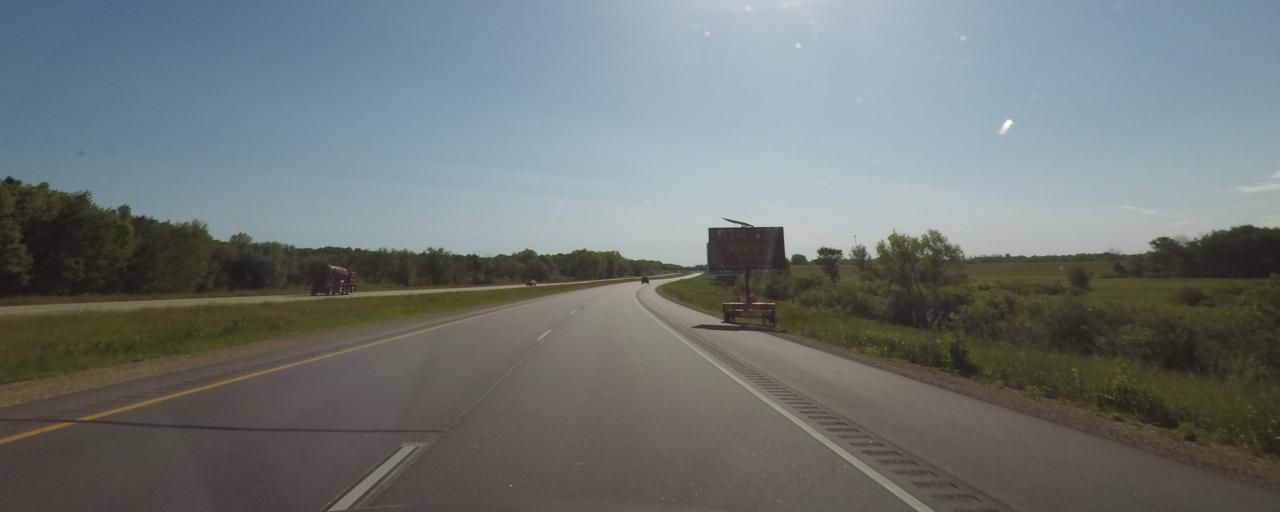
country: US
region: Wisconsin
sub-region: Columbia County
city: Columbus
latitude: 43.3544
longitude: -89.0217
